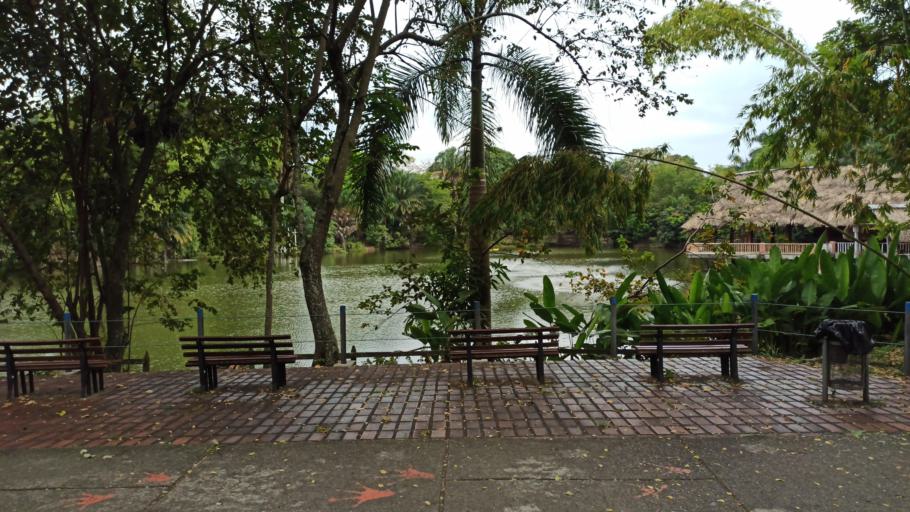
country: CO
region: Valle del Cauca
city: Palmira
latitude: 3.5291
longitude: -76.2880
